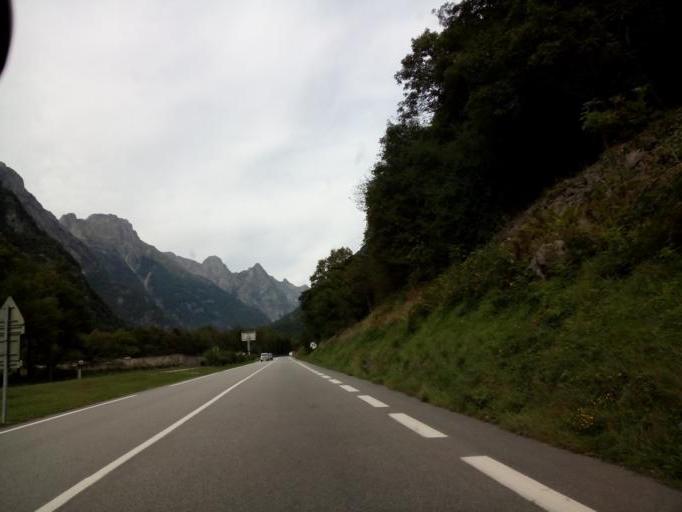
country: FR
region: Rhone-Alpes
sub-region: Departement de l'Isere
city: Livet-et-Gavet
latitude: 45.0765
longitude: 5.8847
